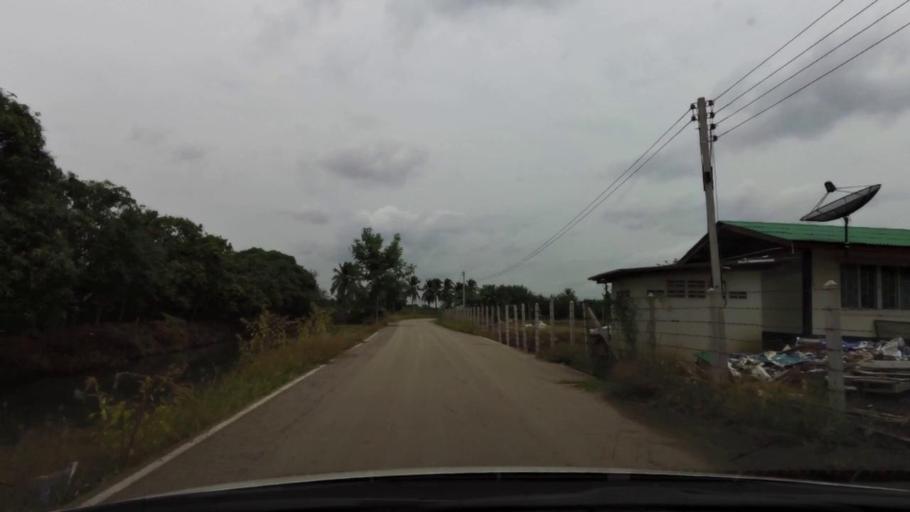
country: TH
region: Samut Sakhon
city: Ban Phaeo
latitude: 13.6124
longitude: 100.0315
